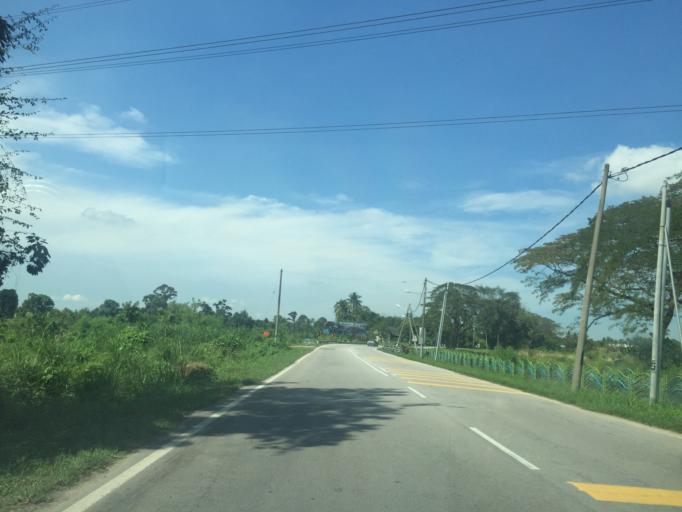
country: MY
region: Penang
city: Tasek Glugor
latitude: 5.4857
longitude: 100.4816
